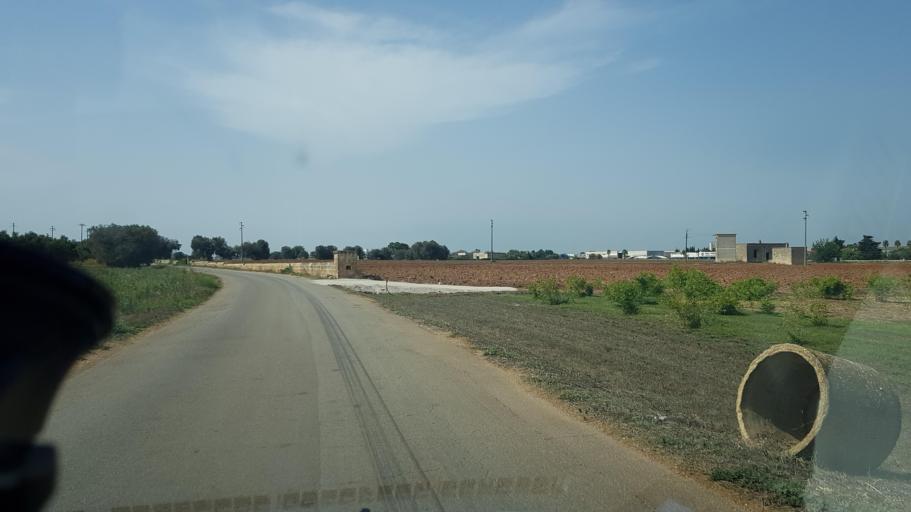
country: IT
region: Apulia
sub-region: Provincia di Brindisi
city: Mesagne
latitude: 40.5734
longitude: 17.8363
